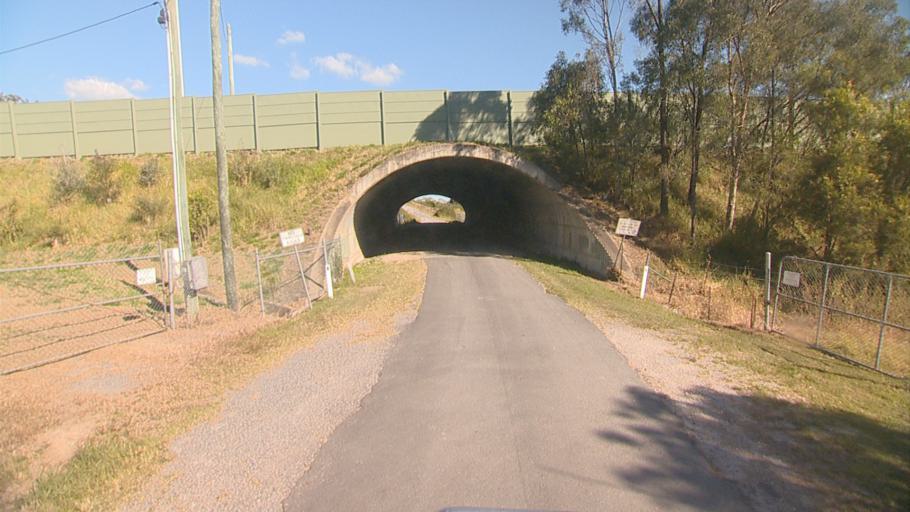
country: AU
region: Queensland
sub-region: Logan
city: Slacks Creek
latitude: -27.6668
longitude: 153.1624
